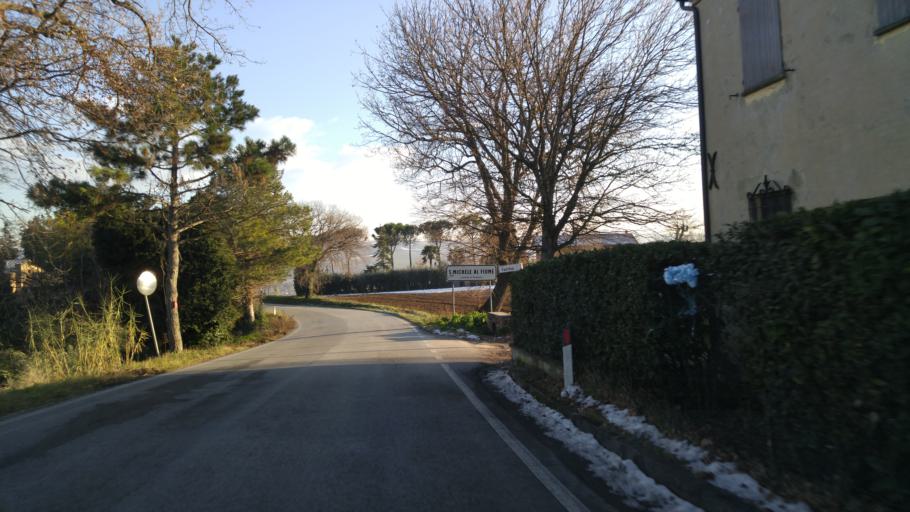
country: IT
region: The Marches
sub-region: Provincia di Pesaro e Urbino
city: San Michele
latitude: 43.6613
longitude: 12.9847
